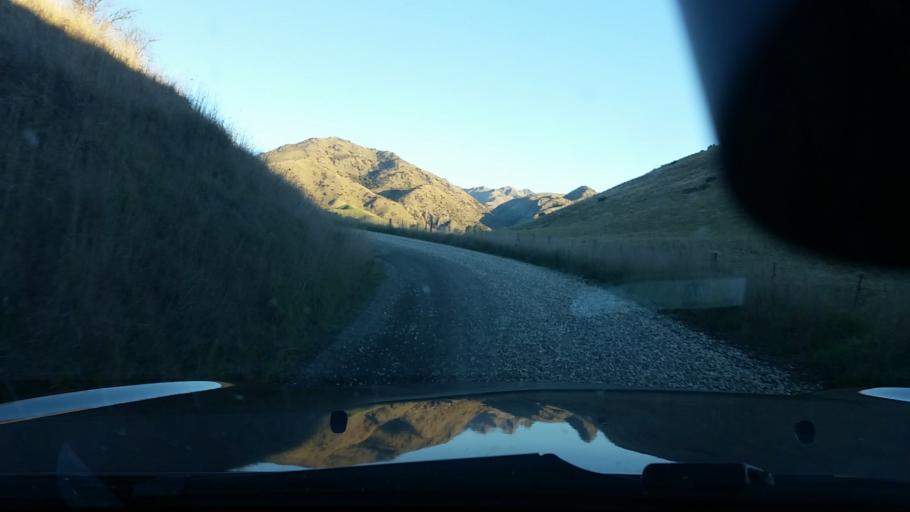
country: NZ
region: Marlborough
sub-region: Marlborough District
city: Blenheim
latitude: -41.7307
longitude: 174.0364
